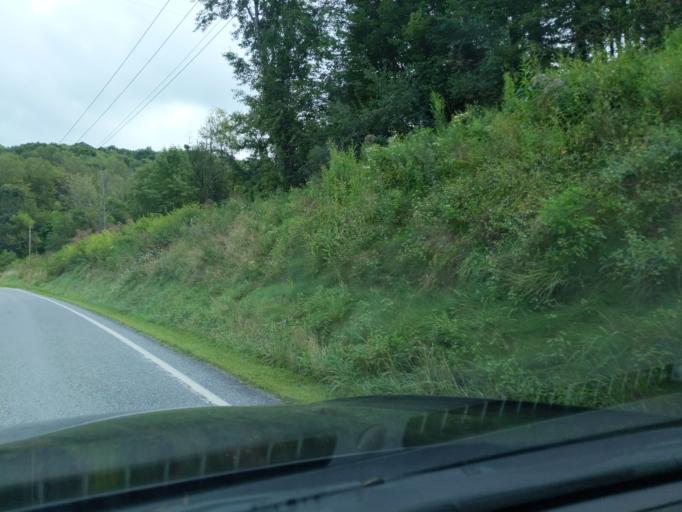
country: US
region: Pennsylvania
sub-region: Blair County
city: Duncansville
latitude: 40.3707
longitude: -78.4979
